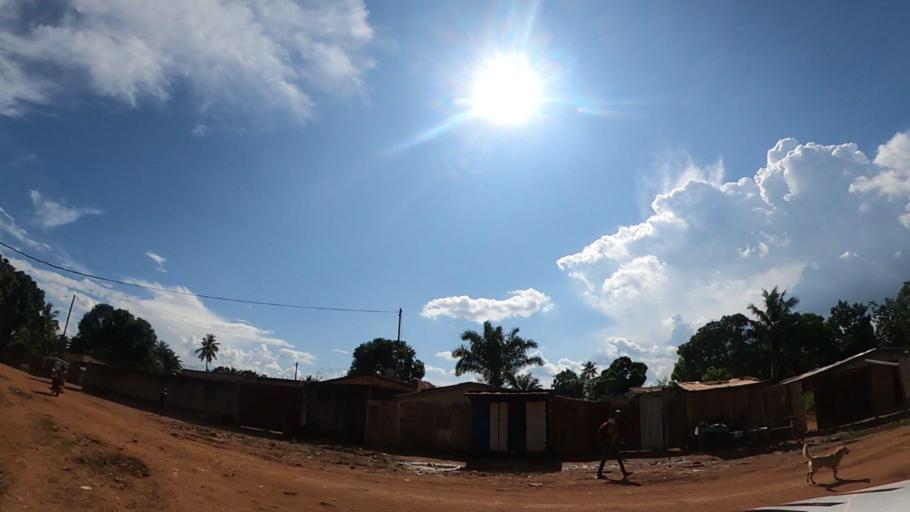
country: CF
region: Bangui
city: Bangui
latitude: 4.3764
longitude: 18.5508
